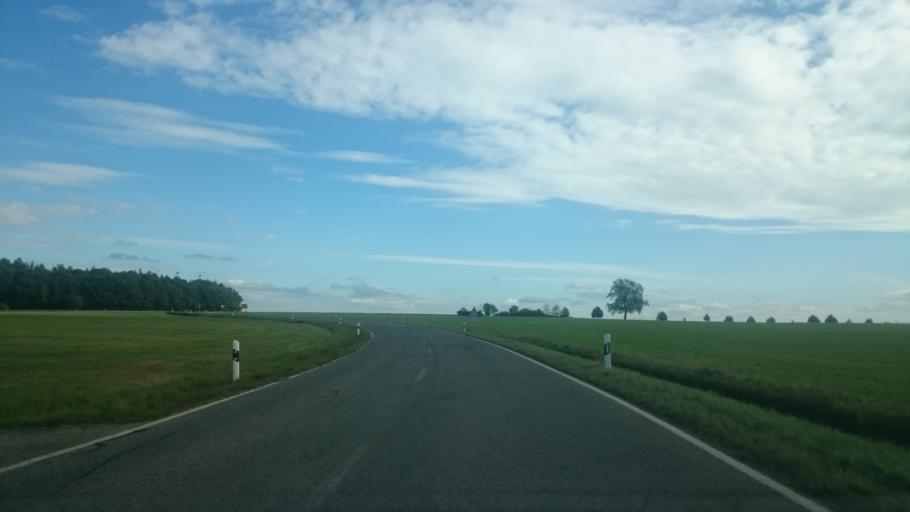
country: DE
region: Bavaria
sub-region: Regierungsbezirk Mittelfranken
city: Thalmassing
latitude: 49.1528
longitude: 11.2537
